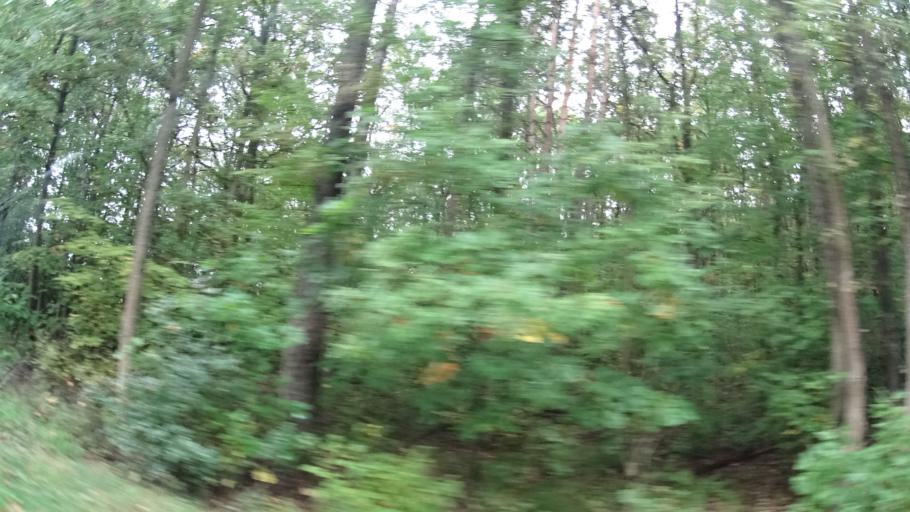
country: DE
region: Bavaria
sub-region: Upper Franconia
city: Breitengussbach
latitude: 49.9717
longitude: 10.9159
